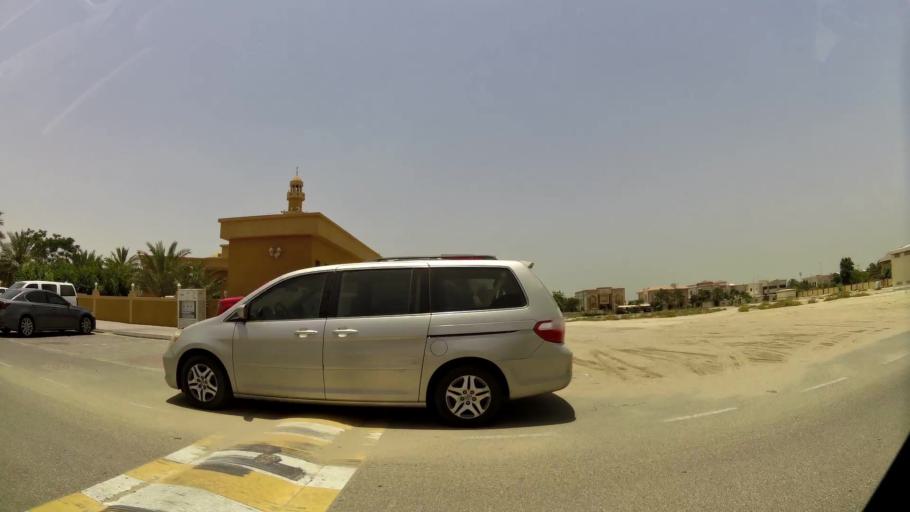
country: AE
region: Ash Shariqah
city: Sharjah
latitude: 25.2103
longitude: 55.3834
